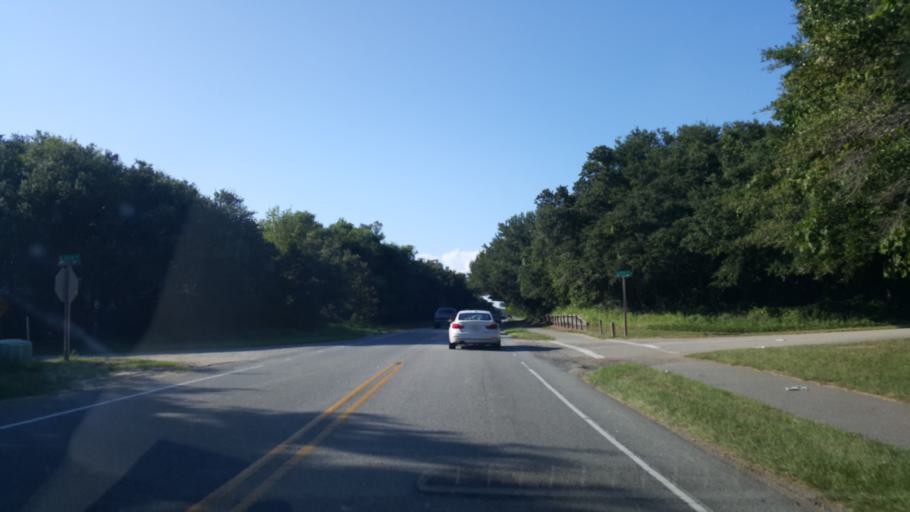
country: US
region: North Carolina
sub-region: Dare County
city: Southern Shores
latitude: 36.1462
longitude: -75.7409
